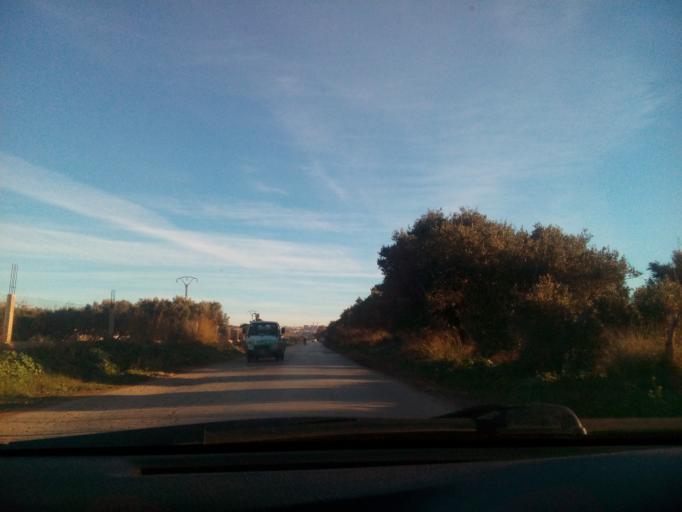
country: DZ
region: Oran
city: Es Senia
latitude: 35.6118
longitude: -0.6883
